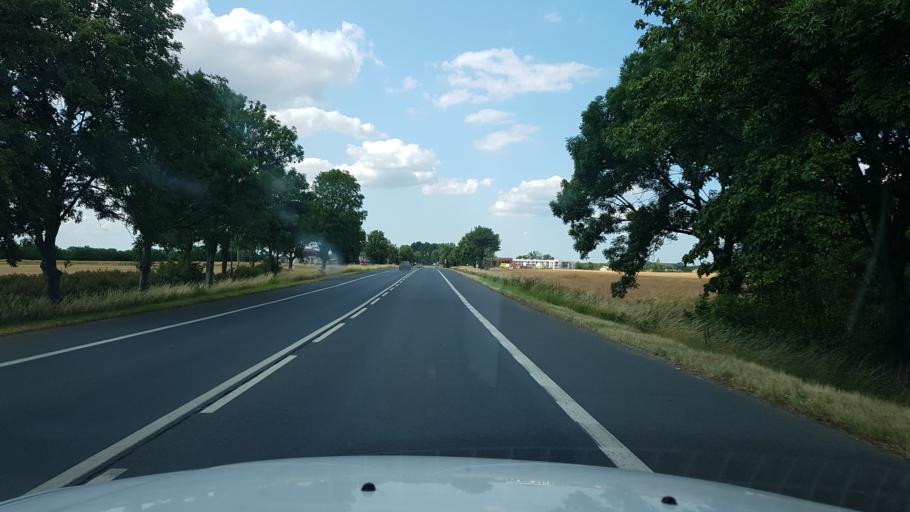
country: PL
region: West Pomeranian Voivodeship
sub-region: Powiat pyrzycki
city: Pyrzyce
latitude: 53.1217
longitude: 14.8909
